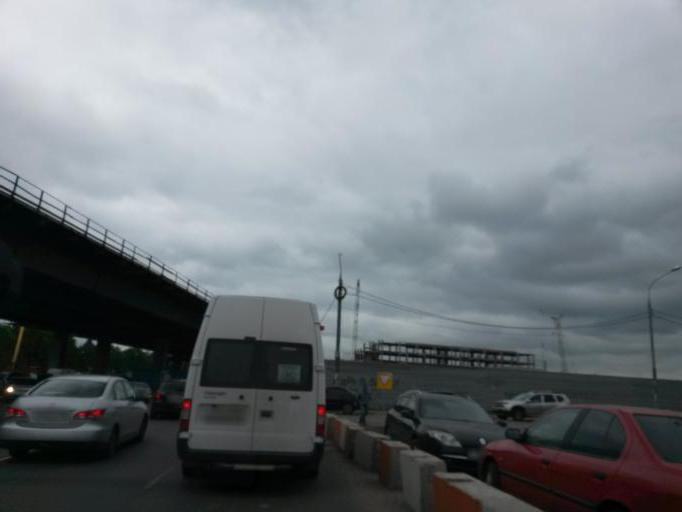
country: RU
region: Moskovskaya
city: Klimovsk
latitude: 55.3833
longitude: 37.5376
